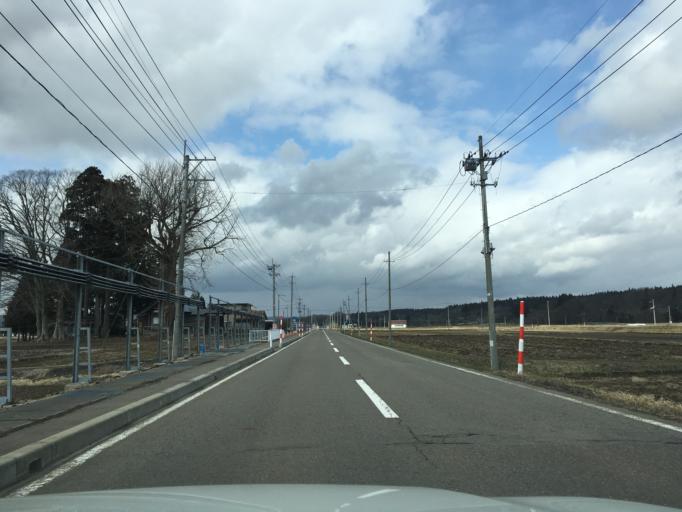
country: JP
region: Akita
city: Takanosu
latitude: 40.1339
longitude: 140.3561
